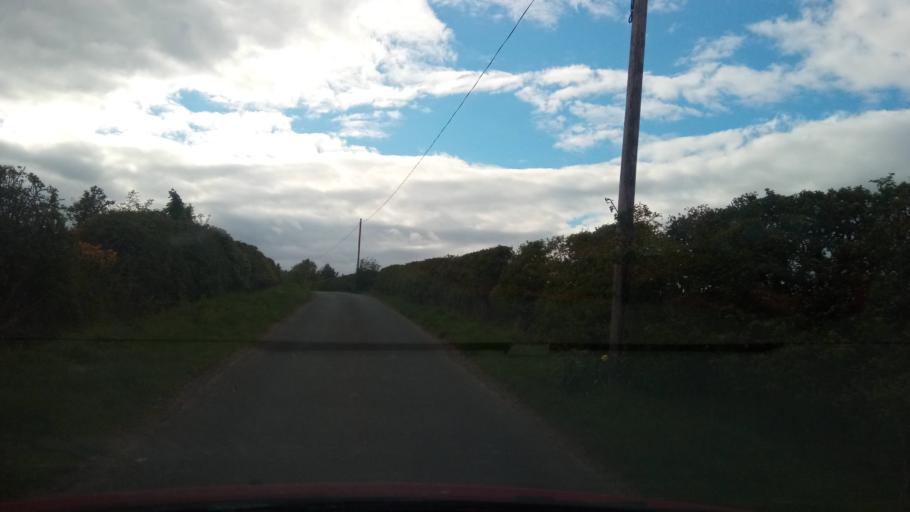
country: GB
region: Scotland
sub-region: The Scottish Borders
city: Saint Boswells
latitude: 55.5089
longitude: -2.6484
